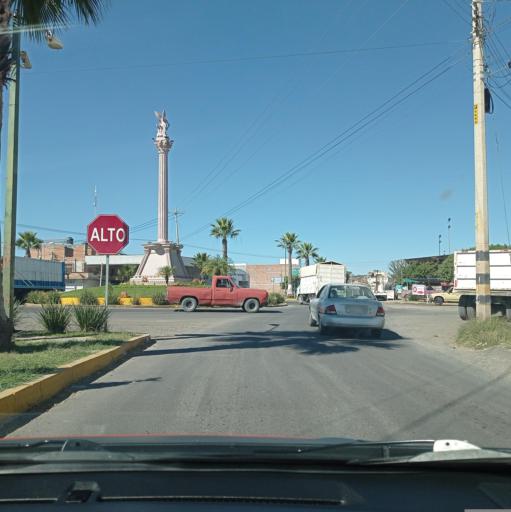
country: MX
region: Jalisco
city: San Miguel el Alto
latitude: 21.0407
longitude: -102.4006
